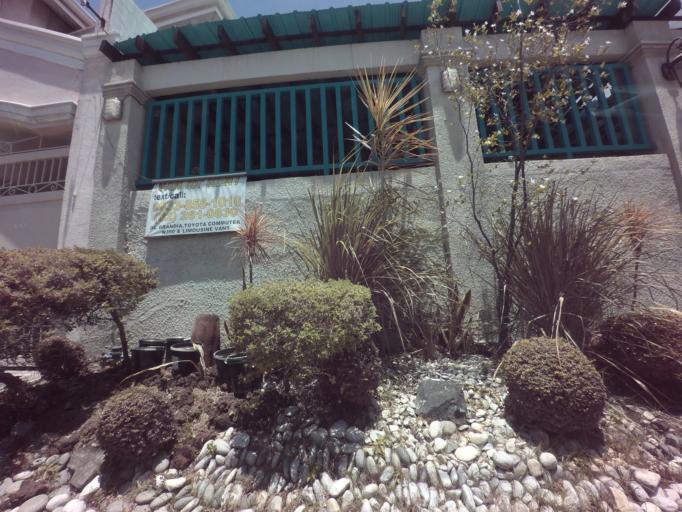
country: PH
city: Sambayanihan People's Village
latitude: 14.4870
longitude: 121.0373
